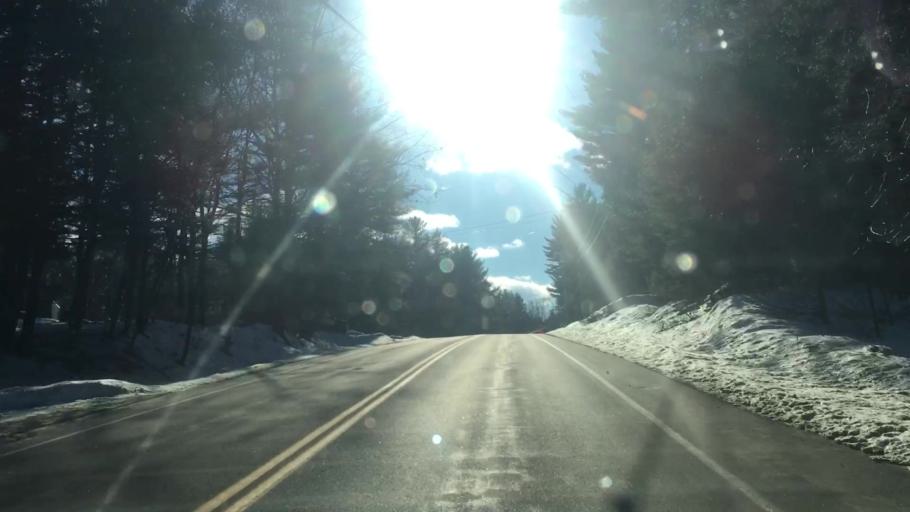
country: US
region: Maine
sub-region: Somerset County
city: Madison
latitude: 44.9413
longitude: -69.8652
